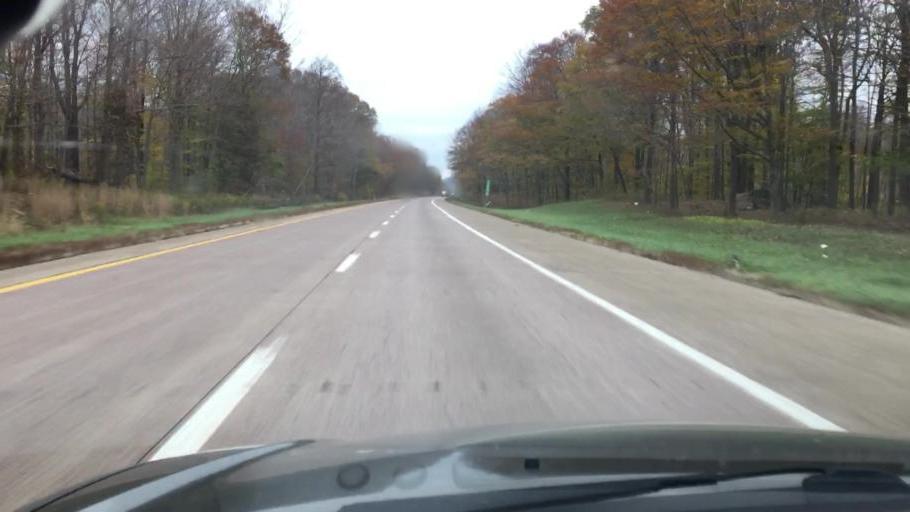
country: US
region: Pennsylvania
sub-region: Luzerne County
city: Freeland
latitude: 41.0590
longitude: -75.9270
